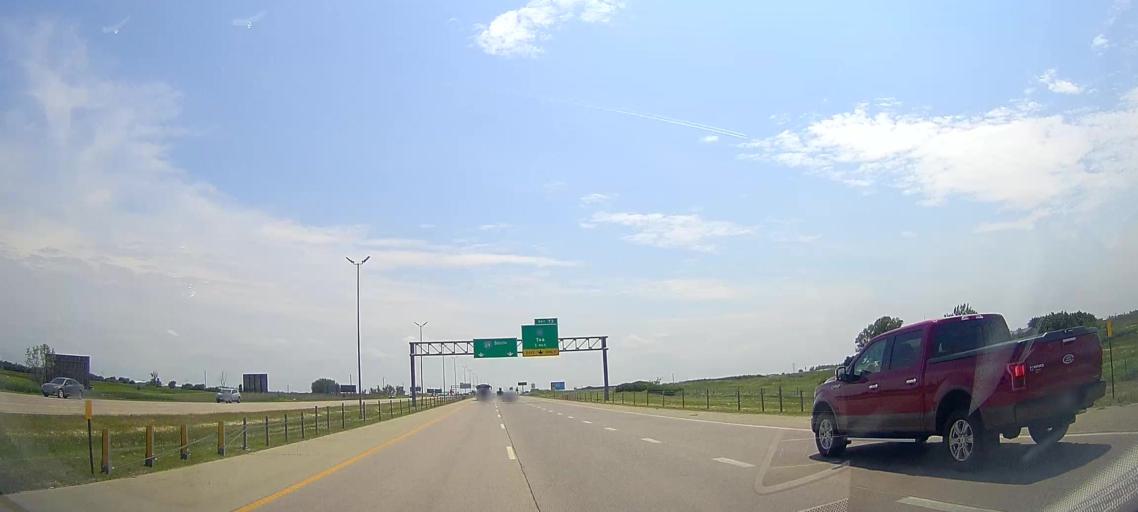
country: US
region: South Dakota
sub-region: Lincoln County
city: Tea
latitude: 43.4776
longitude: -96.7968
